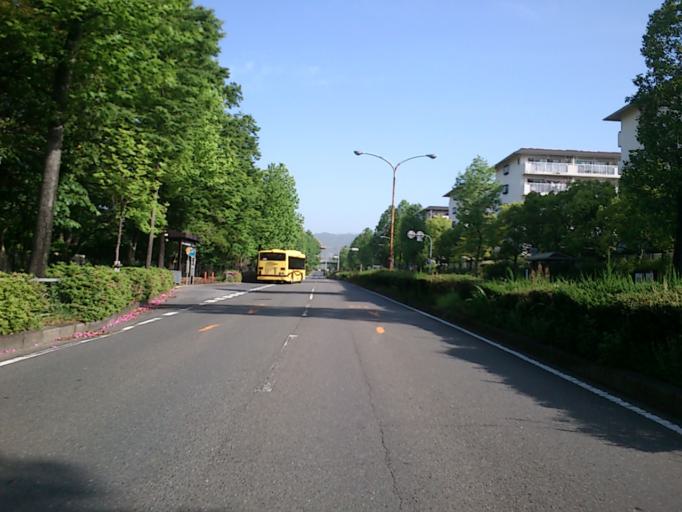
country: JP
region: Kyoto
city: Muko
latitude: 34.9600
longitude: 135.6798
